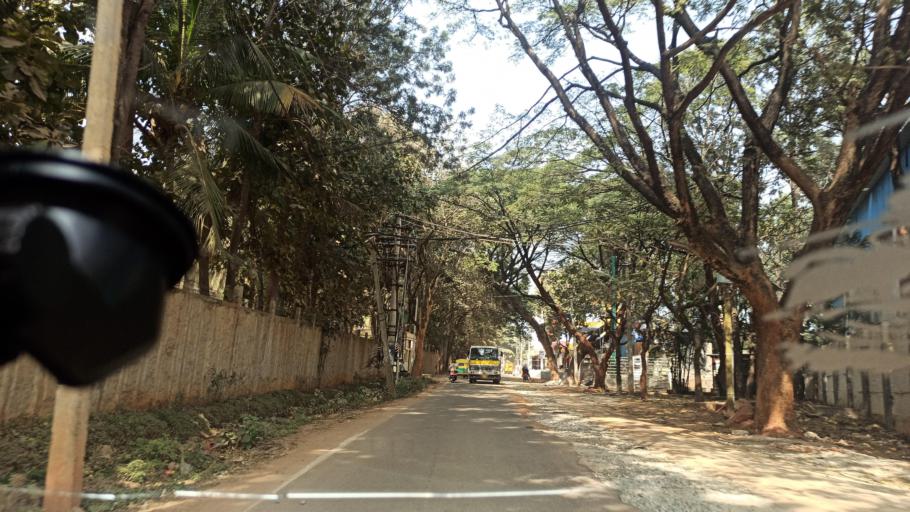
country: IN
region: Karnataka
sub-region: Bangalore Urban
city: Yelahanka
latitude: 13.0933
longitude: 77.6189
